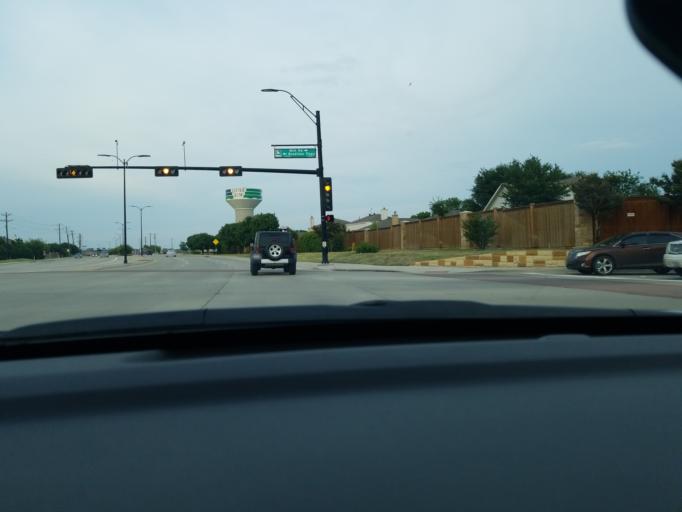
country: US
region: Texas
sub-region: Denton County
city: Little Elm
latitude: 33.1683
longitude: -96.9016
